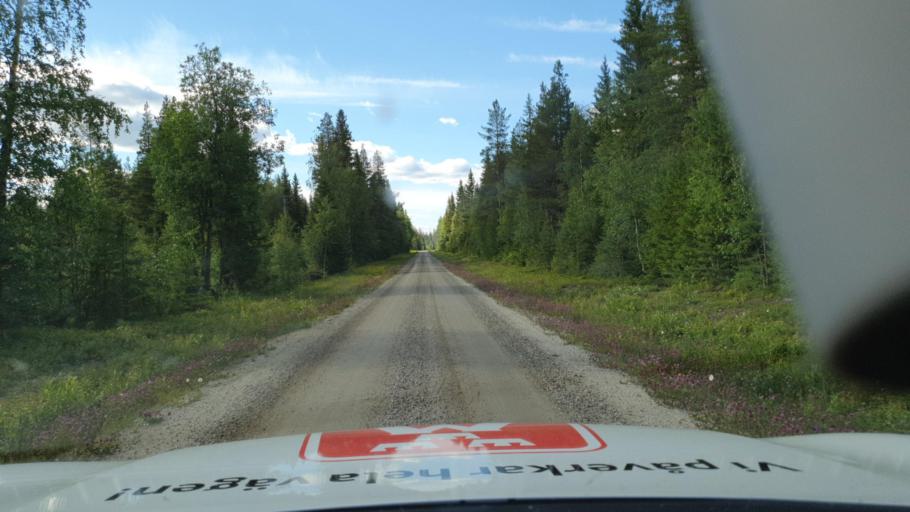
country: SE
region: Vaesterbotten
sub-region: Lycksele Kommun
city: Lycksele
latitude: 64.4605
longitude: 18.3053
